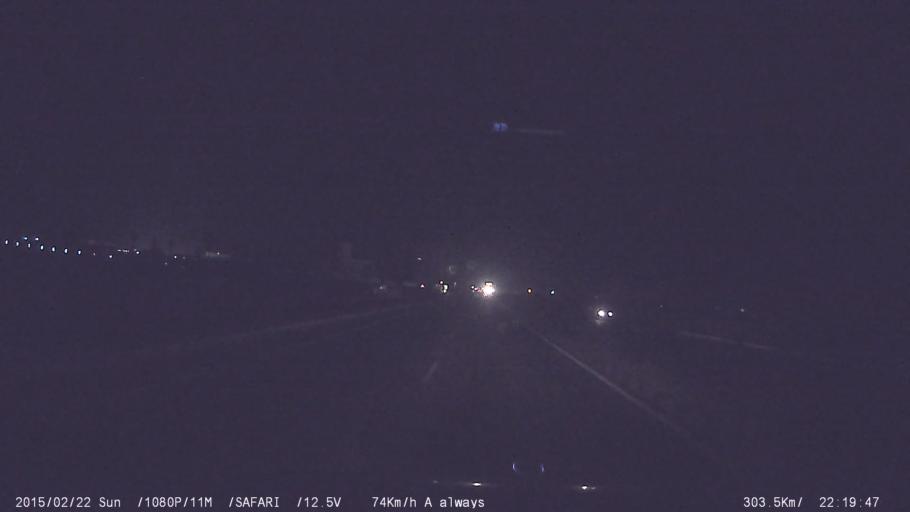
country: IN
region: Tamil Nadu
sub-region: Karur
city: Karur
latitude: 10.9837
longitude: 78.0647
